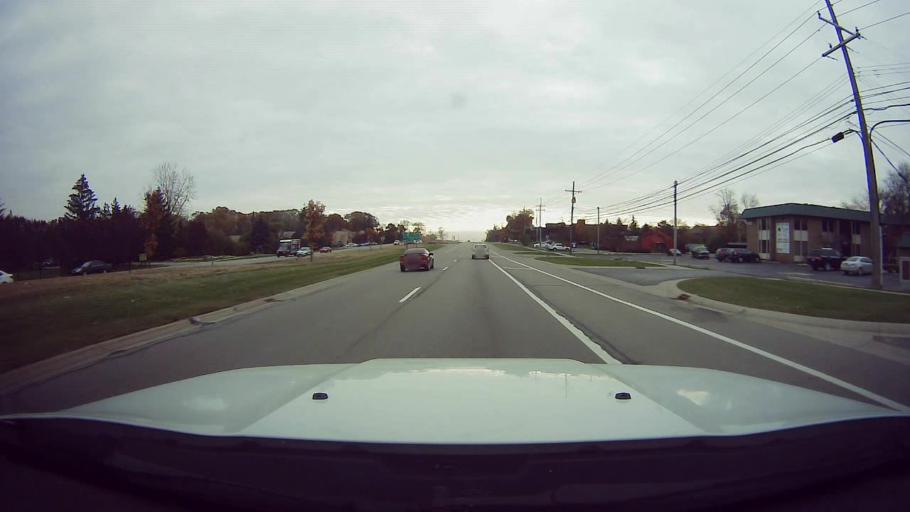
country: US
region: Michigan
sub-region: Oakland County
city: Franklin
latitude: 42.5179
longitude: -83.3386
